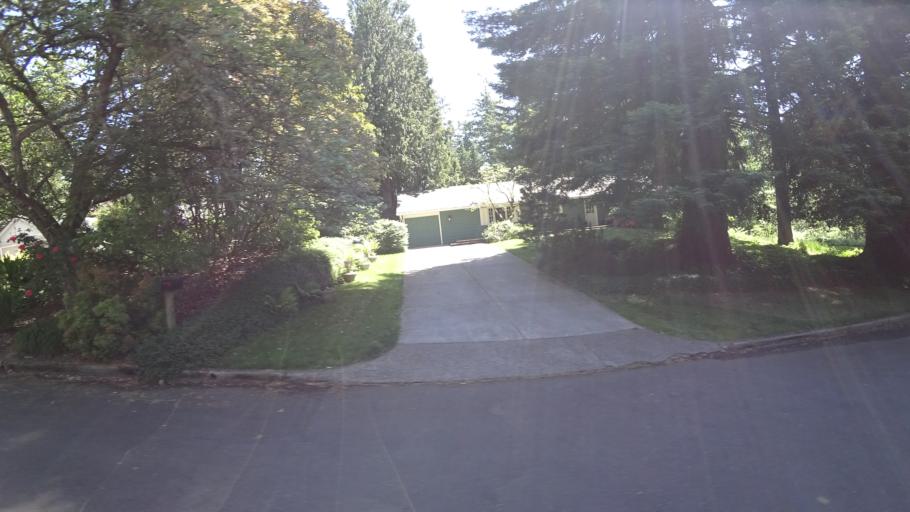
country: US
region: Oregon
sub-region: Washington County
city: Raleigh Hills
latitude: 45.4874
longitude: -122.7136
